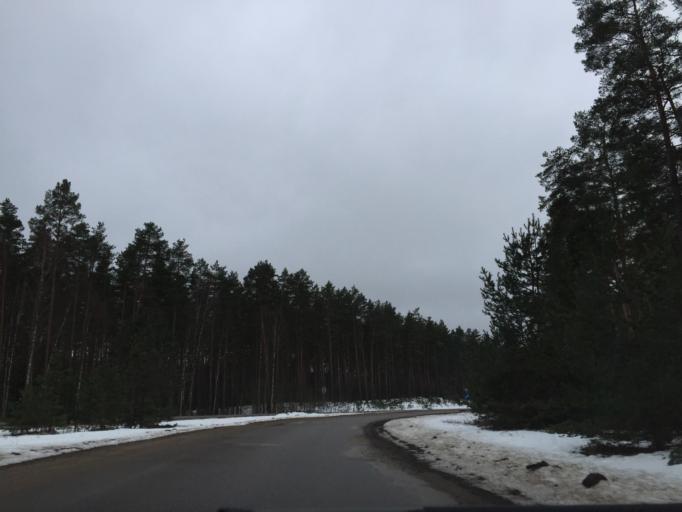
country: LV
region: Incukalns
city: Vangazi
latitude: 57.0806
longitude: 24.5198
